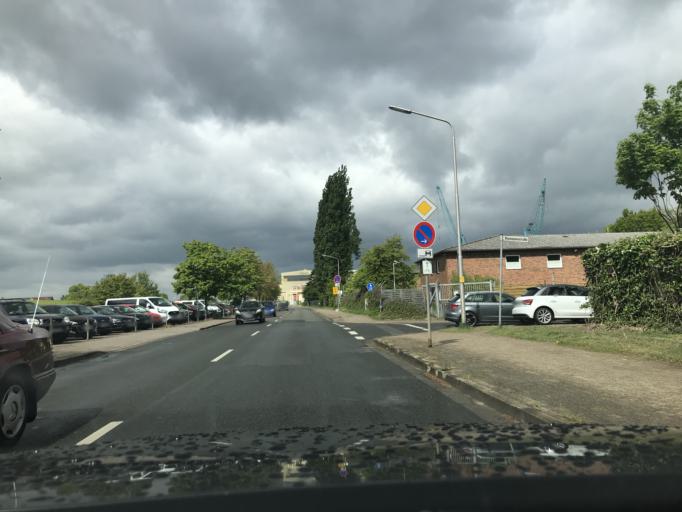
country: DE
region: Lower Saxony
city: Lemwerder
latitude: 53.1660
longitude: 8.6145
